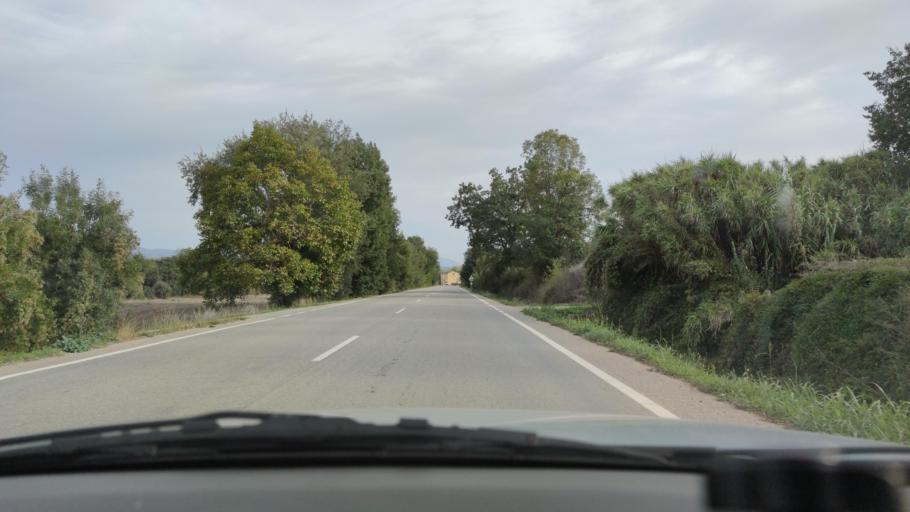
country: ES
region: Catalonia
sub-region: Provincia de Lleida
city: Artesa de Segre
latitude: 41.9041
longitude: 1.0666
